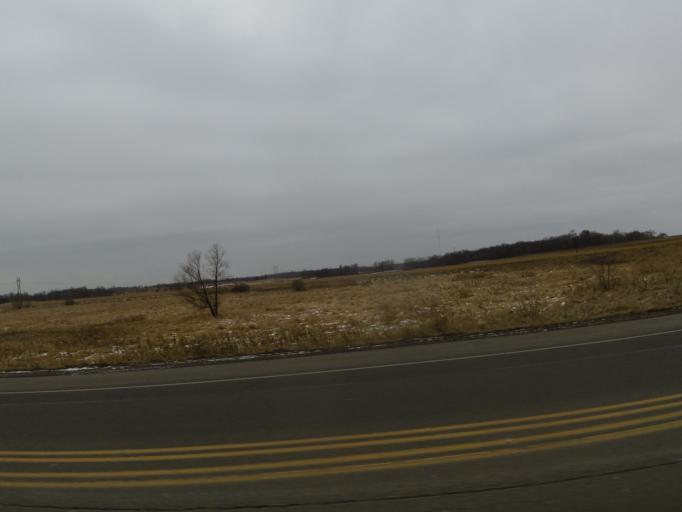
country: US
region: Minnesota
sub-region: Wright County
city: Delano
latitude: 45.0610
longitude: -93.8069
